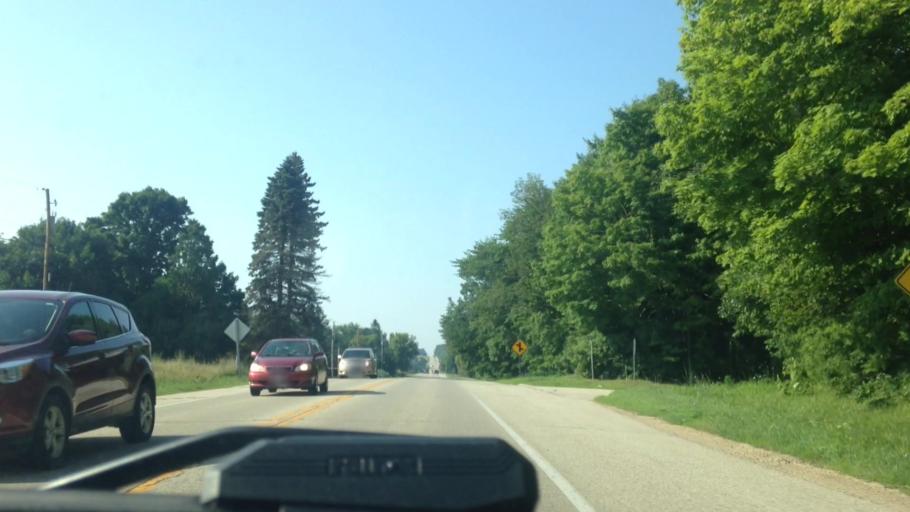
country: US
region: Wisconsin
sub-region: Washington County
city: Richfield
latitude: 43.2492
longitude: -88.2618
